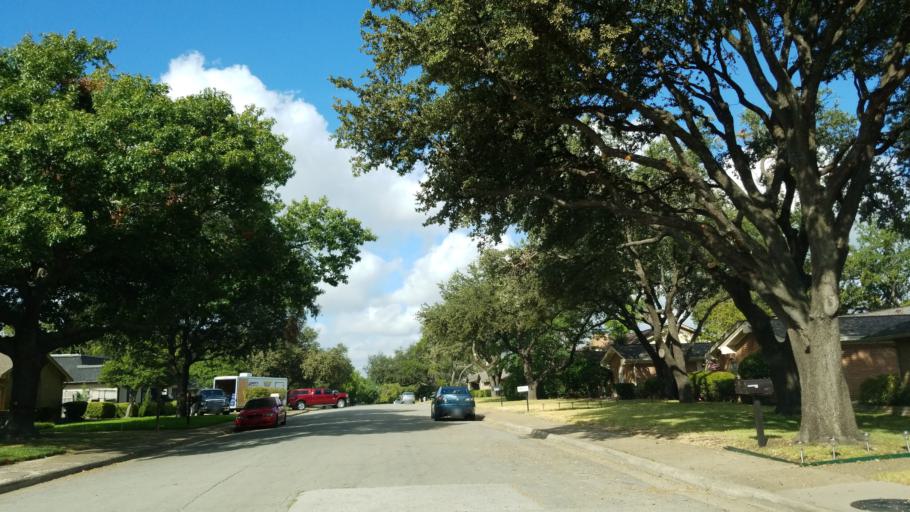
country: US
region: Texas
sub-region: Dallas County
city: Richardson
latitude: 32.9488
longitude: -96.7731
